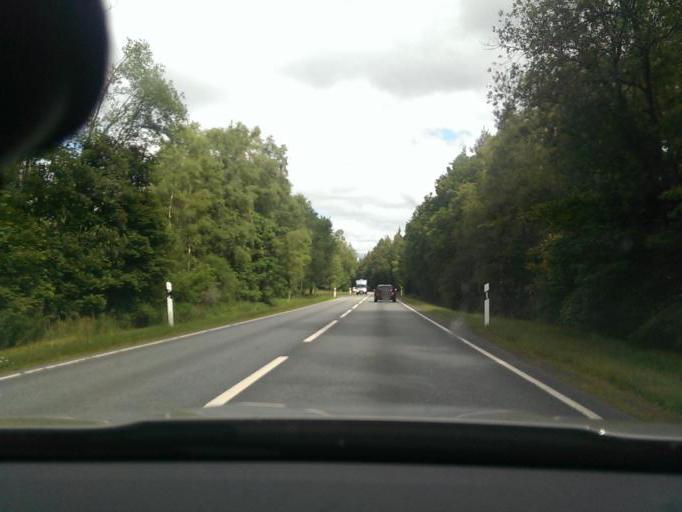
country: SE
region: Joenkoeping
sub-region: Gnosjo Kommun
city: Hillerstorp
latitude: 57.2779
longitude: 13.9691
